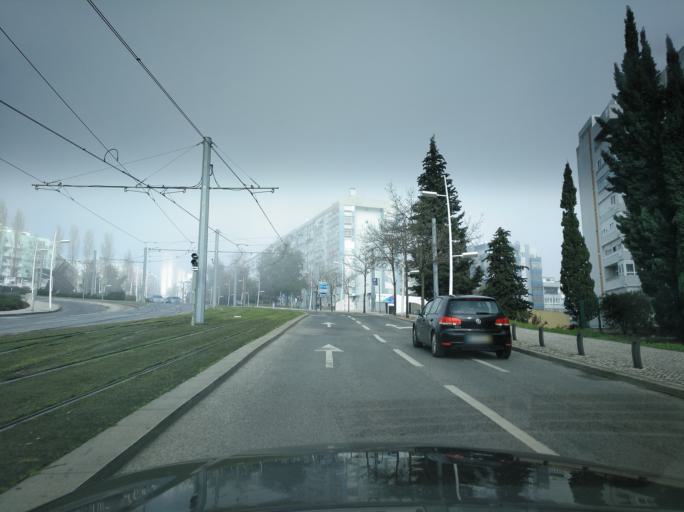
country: PT
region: Setubal
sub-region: Almada
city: Pragal
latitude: 38.6686
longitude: -9.1658
